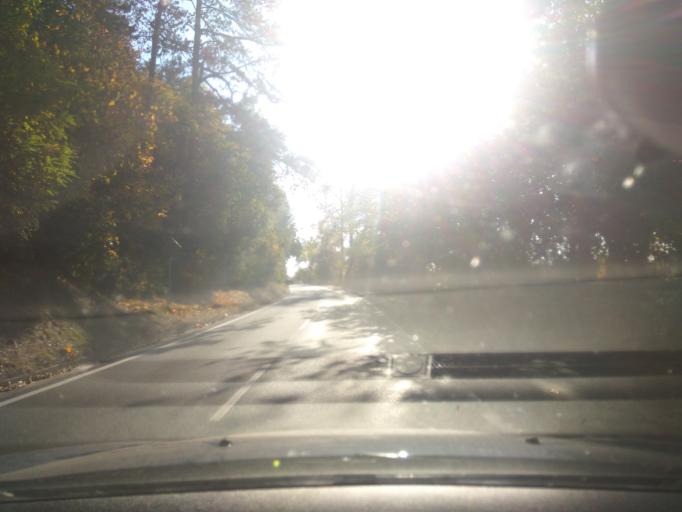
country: SK
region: Trnavsky
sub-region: Okres Trnava
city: Piestany
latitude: 48.5823
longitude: 17.8367
